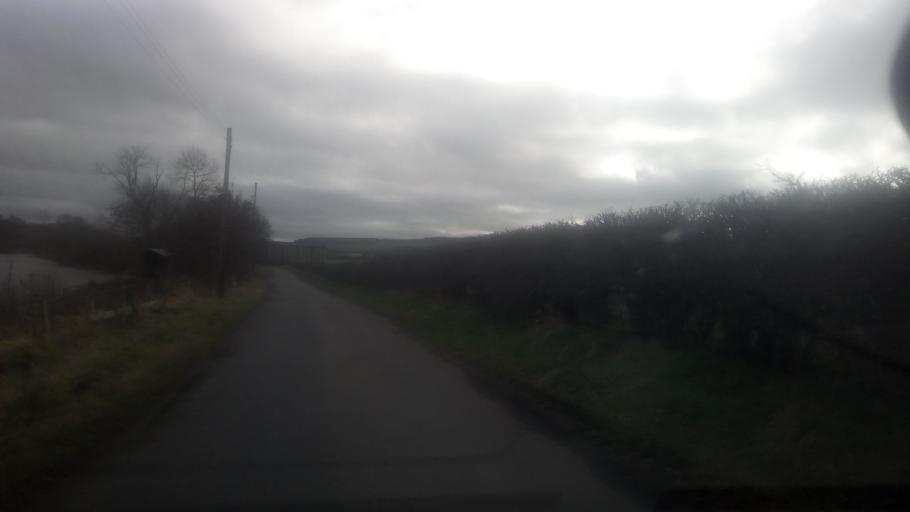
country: GB
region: Scotland
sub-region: The Scottish Borders
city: Kelso
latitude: 55.5458
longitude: -2.4748
